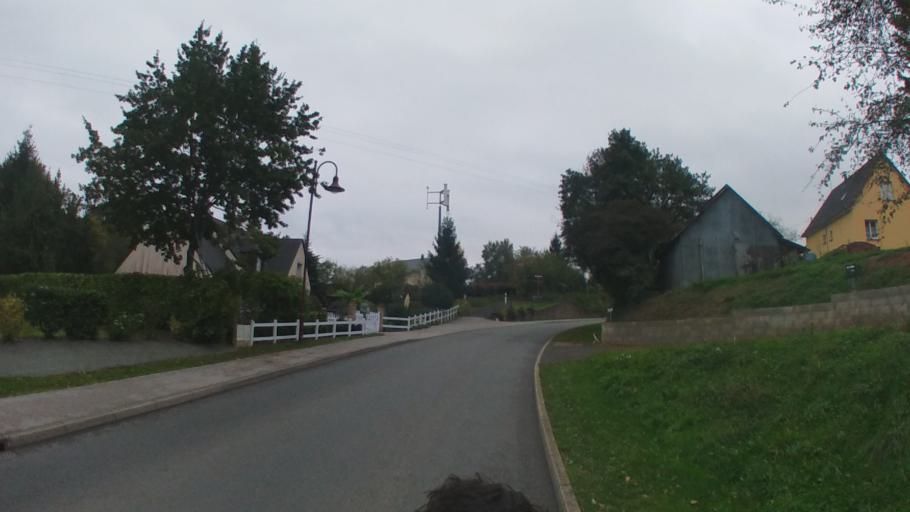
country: FR
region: Pays de la Loire
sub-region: Departement de la Mayenne
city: Aron
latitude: 48.3487
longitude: -0.5784
